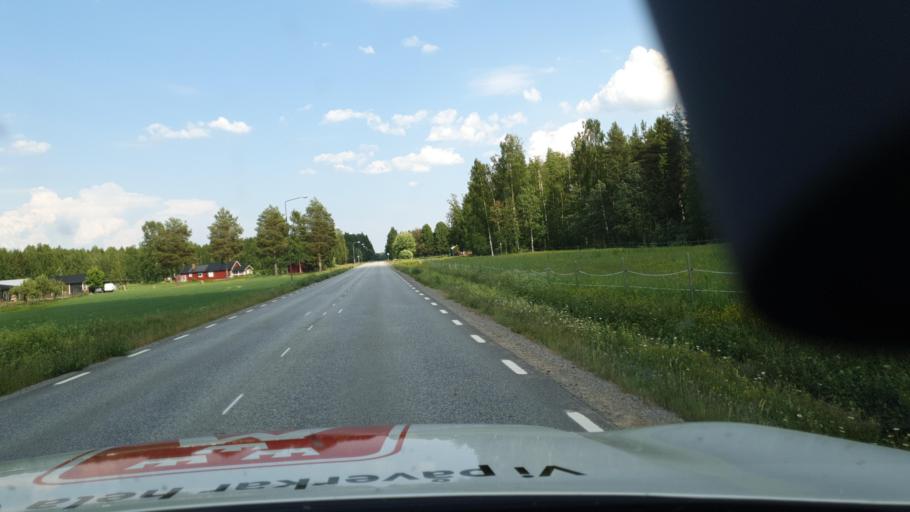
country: SE
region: Vaesterbotten
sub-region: Skelleftea Kommun
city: Viken
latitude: 64.7405
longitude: 20.7975
